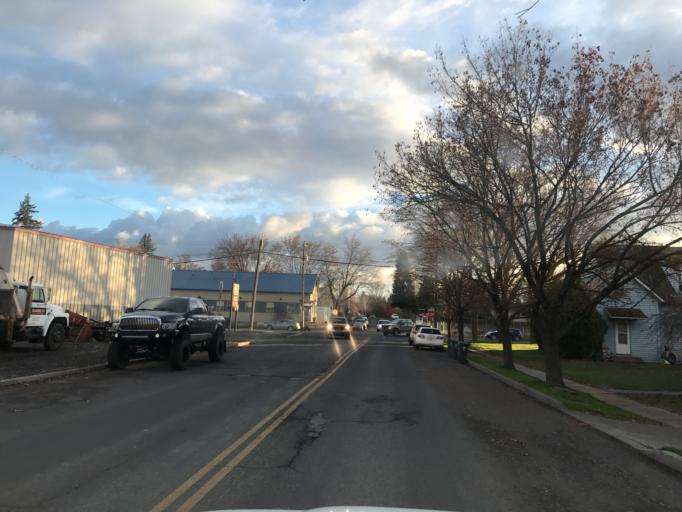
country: US
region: Idaho
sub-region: Latah County
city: Moscow
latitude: 46.7352
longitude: -117.0042
